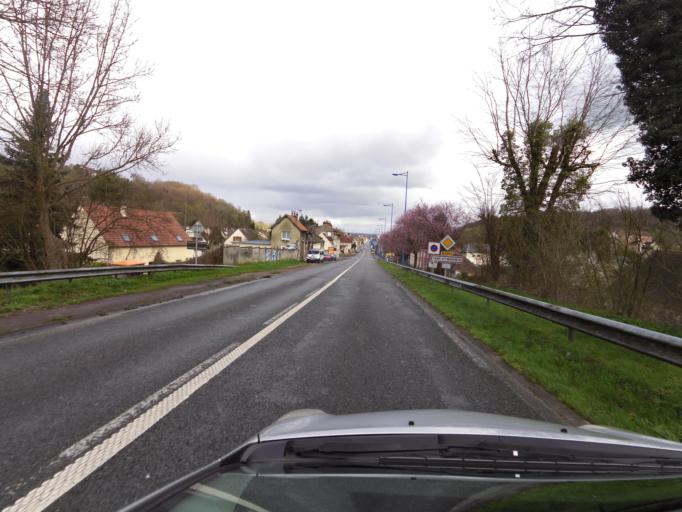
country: FR
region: Picardie
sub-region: Departement de l'Oise
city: Pont-Sainte-Maxence
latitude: 49.2919
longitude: 2.6049
